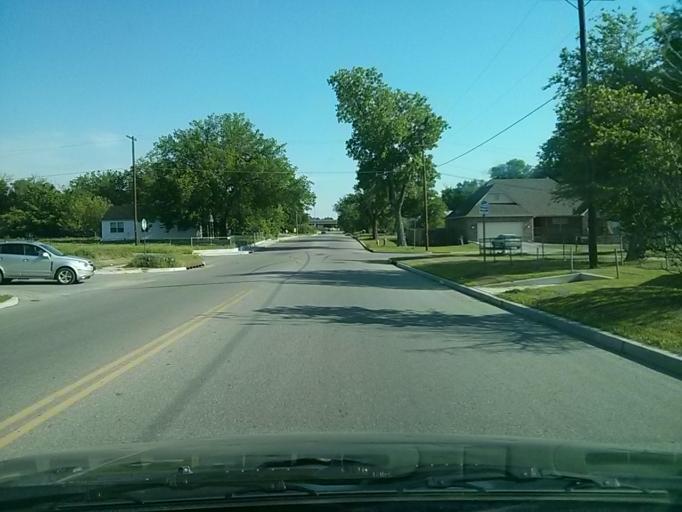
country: US
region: Oklahoma
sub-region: Tulsa County
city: Tulsa
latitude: 36.1946
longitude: -95.9867
